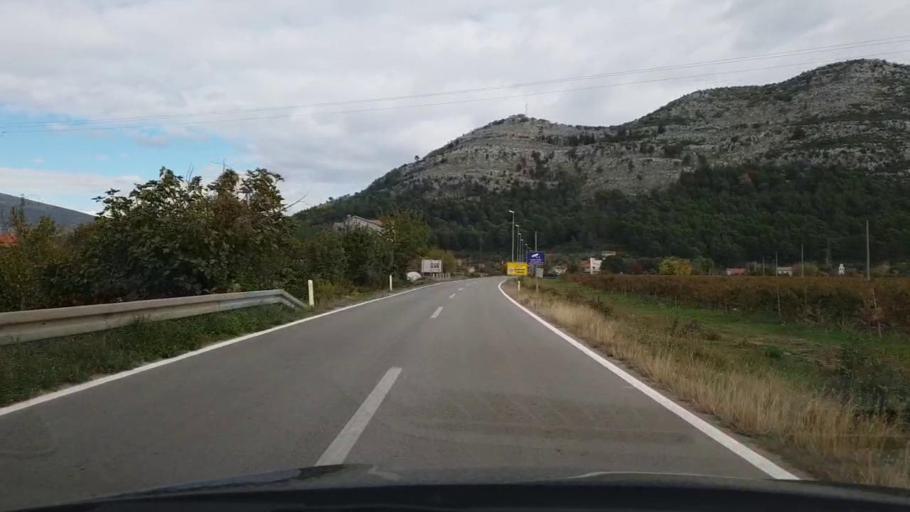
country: BA
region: Republika Srpska
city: Trebinje
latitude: 42.6878
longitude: 18.3301
